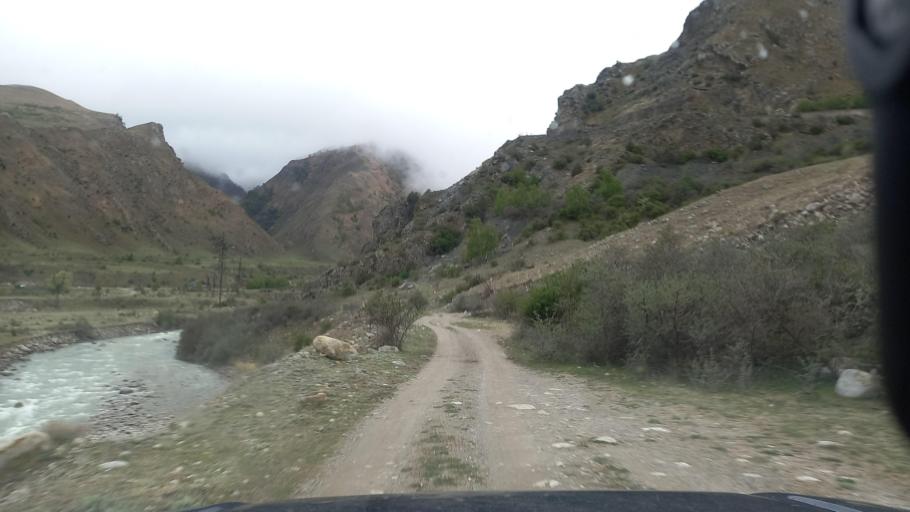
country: RU
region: Kabardino-Balkariya
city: Bylym
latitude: 43.4568
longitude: 43.0096
